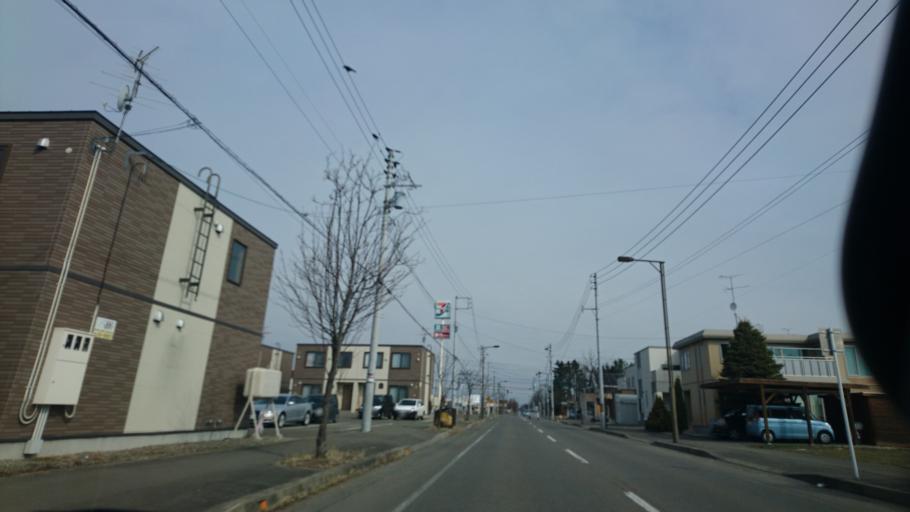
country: JP
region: Hokkaido
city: Otofuke
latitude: 42.9717
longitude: 143.2125
